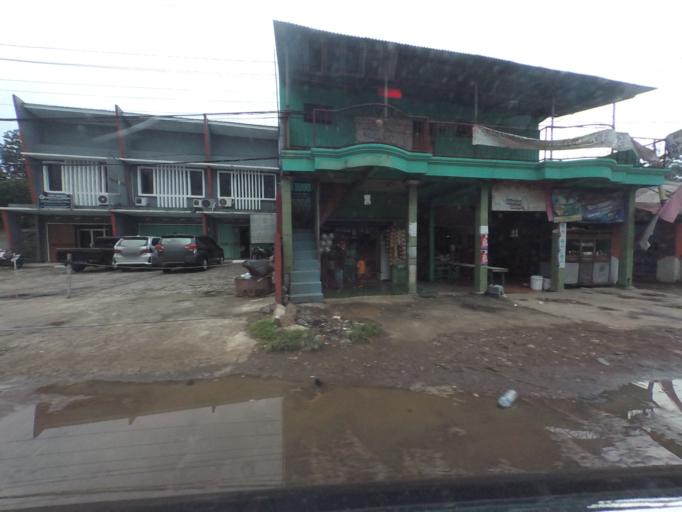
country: ID
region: West Java
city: Cicurug
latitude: -6.8338
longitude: 106.7612
